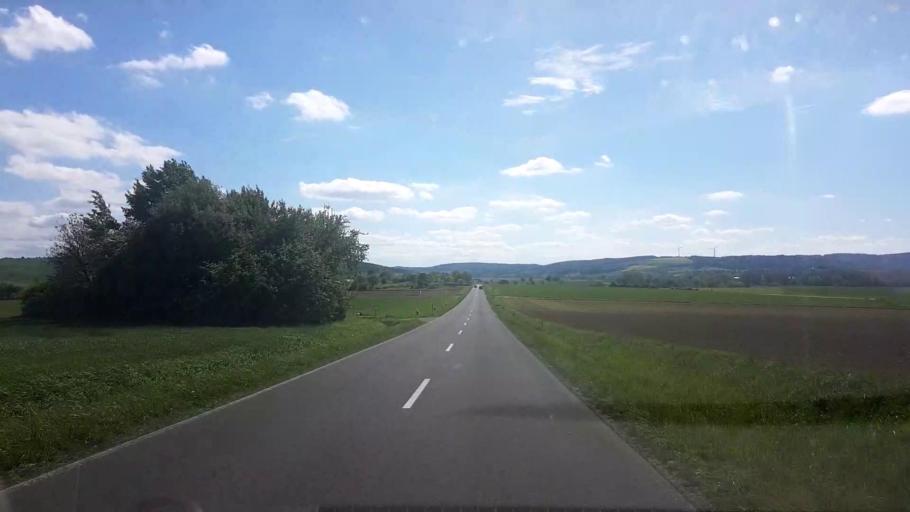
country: DE
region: Bavaria
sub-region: Regierungsbezirk Unterfranken
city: Untermerzbach
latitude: 50.1425
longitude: 10.8880
